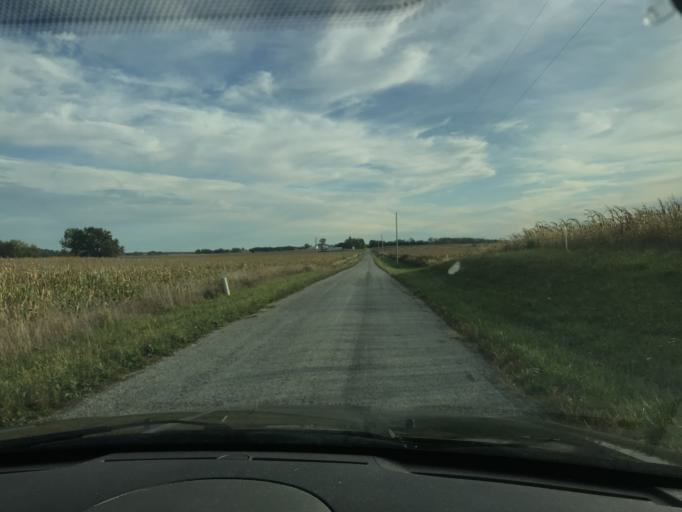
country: US
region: Ohio
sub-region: Logan County
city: West Liberty
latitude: 40.2158
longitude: -83.8079
